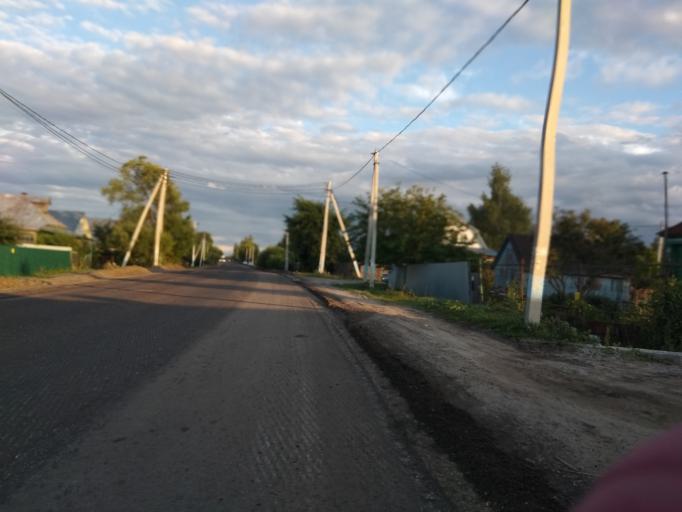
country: RU
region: Moskovskaya
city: Misheronskiy
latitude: 55.6544
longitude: 39.7525
